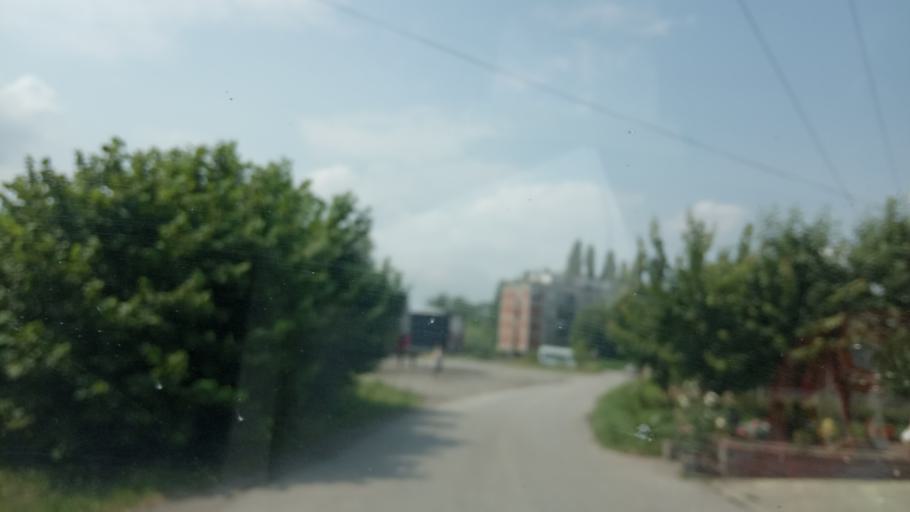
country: RS
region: Central Serbia
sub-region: Belgrade
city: Palilula
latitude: 44.8429
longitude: 20.5034
